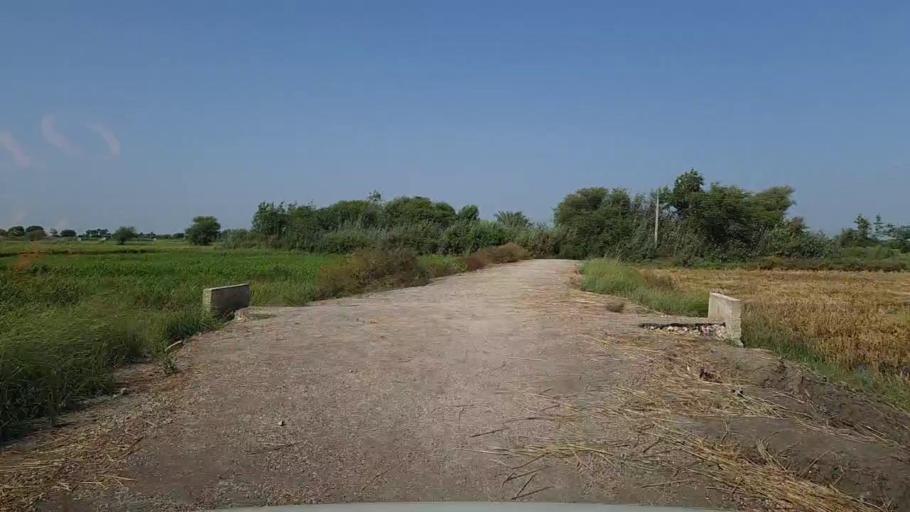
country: PK
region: Sindh
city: Kario
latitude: 24.8535
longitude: 68.6353
